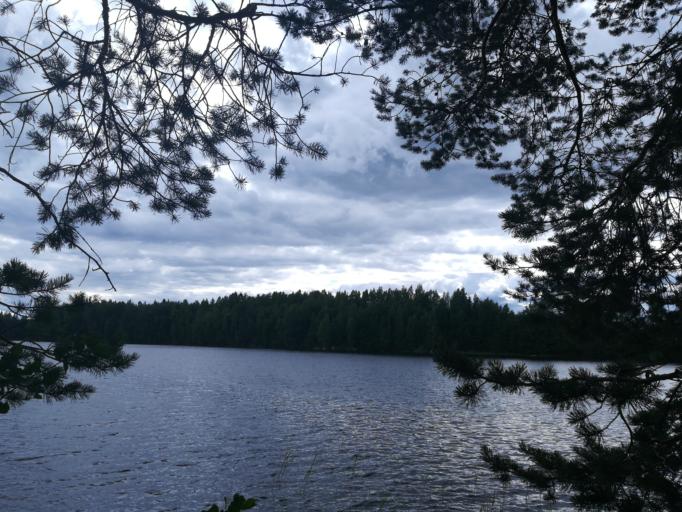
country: FI
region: Southern Savonia
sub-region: Mikkeli
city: Mikkeli
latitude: 61.6708
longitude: 27.1115
